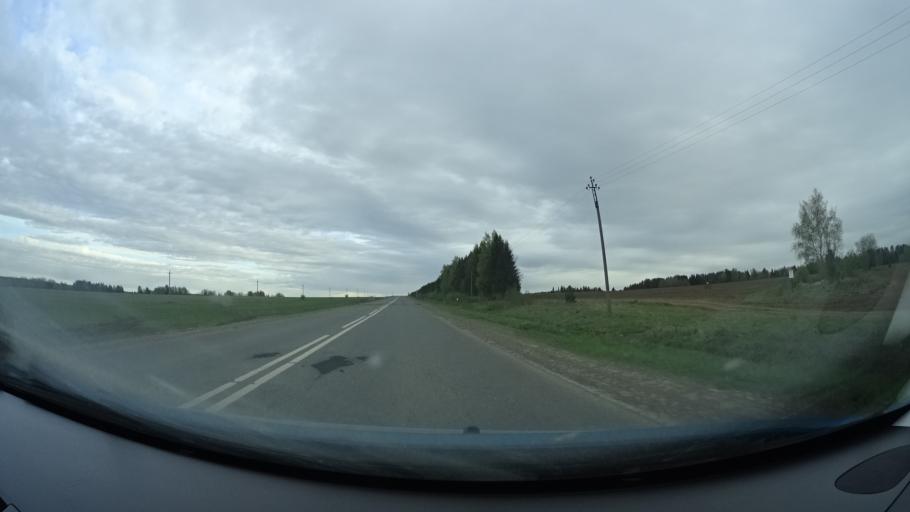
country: RU
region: Perm
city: Osa
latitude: 57.2781
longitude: 55.5670
